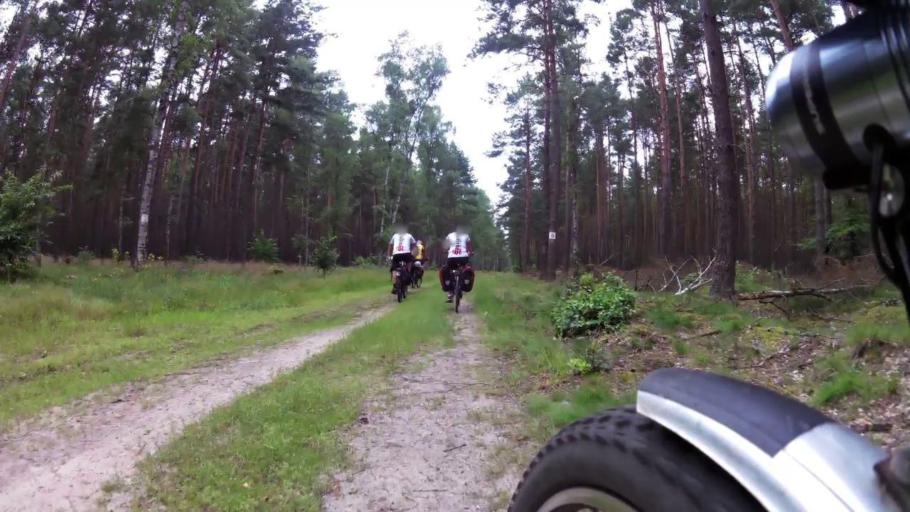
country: PL
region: West Pomeranian Voivodeship
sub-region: Powiat mysliborski
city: Debno
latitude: 52.8298
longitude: 14.6306
